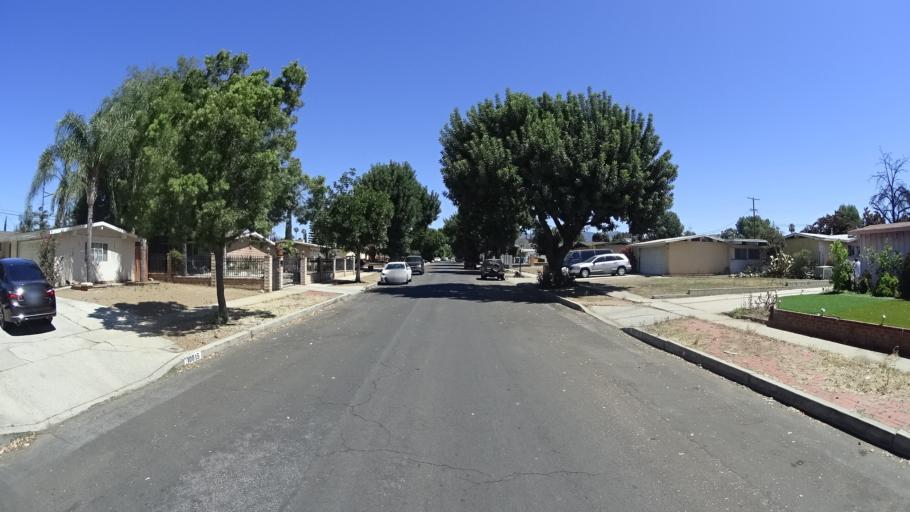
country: US
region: California
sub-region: Los Angeles County
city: San Fernando
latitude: 34.2520
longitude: -118.4555
